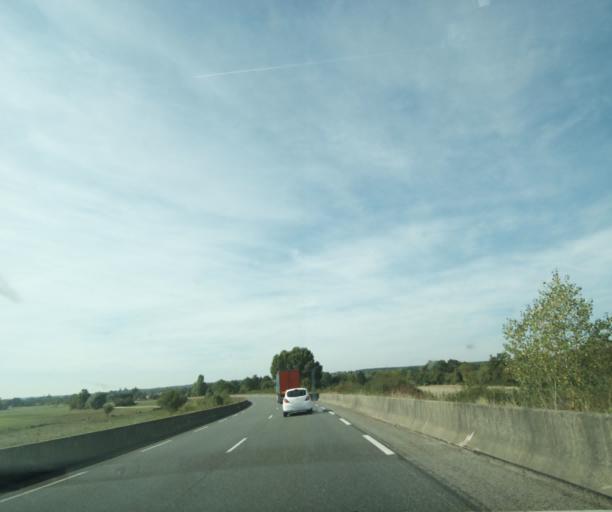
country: FR
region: Auvergne
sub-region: Departement de l'Allier
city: Saint-Remy-en-Rollat
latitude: 46.1925
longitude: 3.4109
